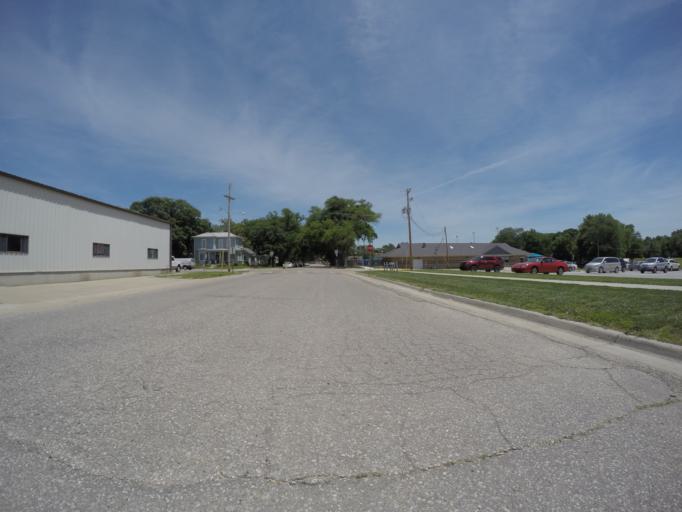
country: US
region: Kansas
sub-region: Marshall County
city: Marysville
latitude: 39.8398
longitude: -96.6486
